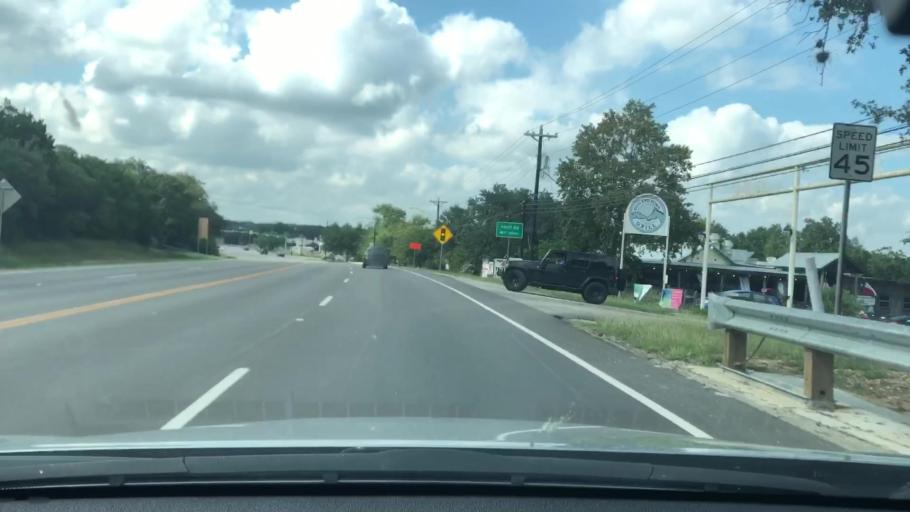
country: US
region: Texas
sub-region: Kendall County
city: Boerne
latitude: 29.7738
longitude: -98.7216
